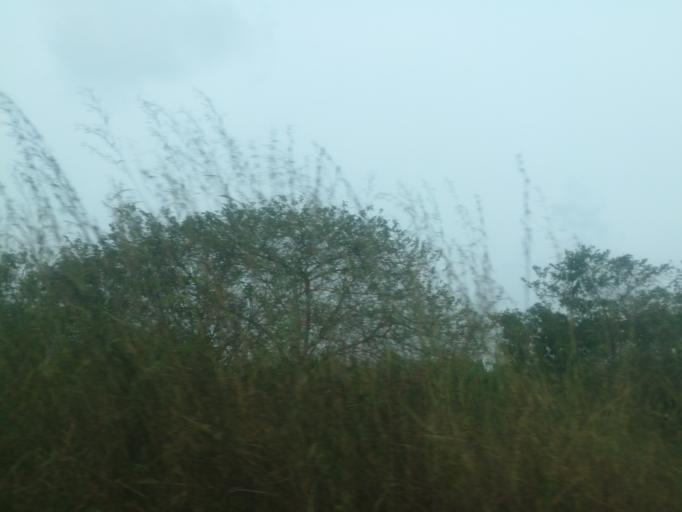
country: NG
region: Ogun
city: Ayetoro
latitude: 7.2808
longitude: 3.0919
